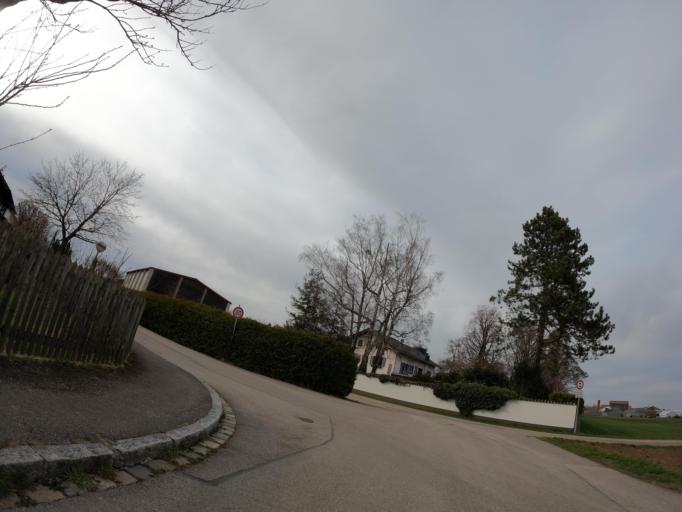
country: DE
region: Bavaria
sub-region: Upper Bavaria
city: Taufkirchen
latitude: 48.0347
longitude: 11.6181
